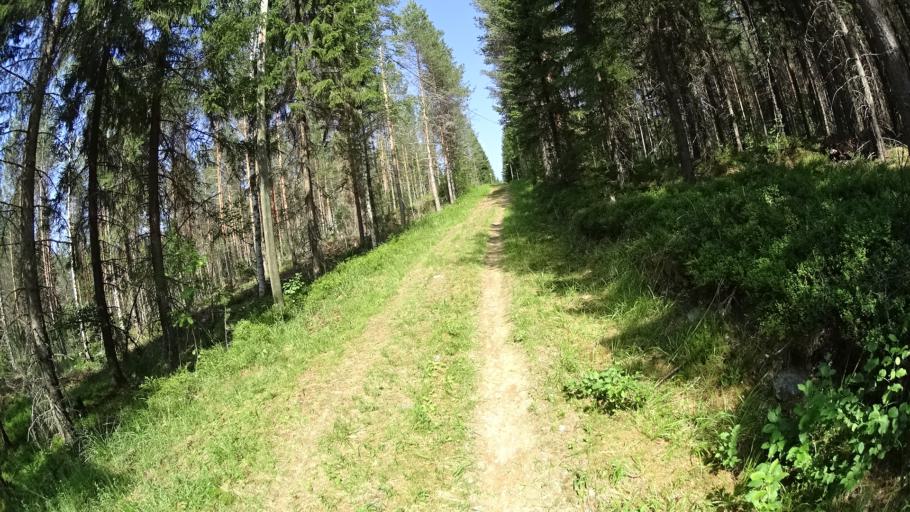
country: FI
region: North Karelia
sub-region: Pielisen Karjala
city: Lieksa
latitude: 63.1253
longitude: 29.8001
